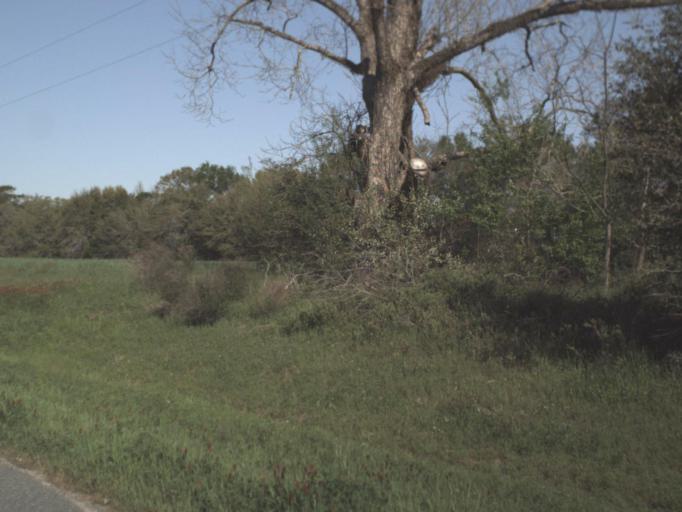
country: US
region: Florida
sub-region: Jackson County
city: Malone
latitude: 30.9603
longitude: -85.2065
